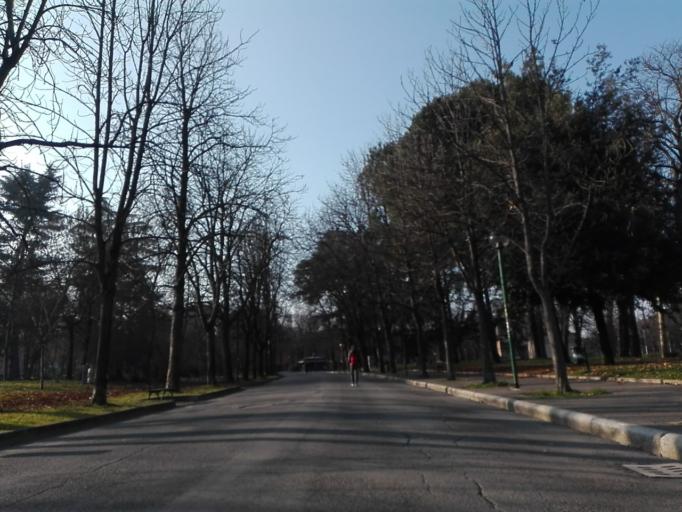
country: IT
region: Emilia-Romagna
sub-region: Provincia di Bologna
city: Bologna
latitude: 44.4846
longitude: 11.3522
